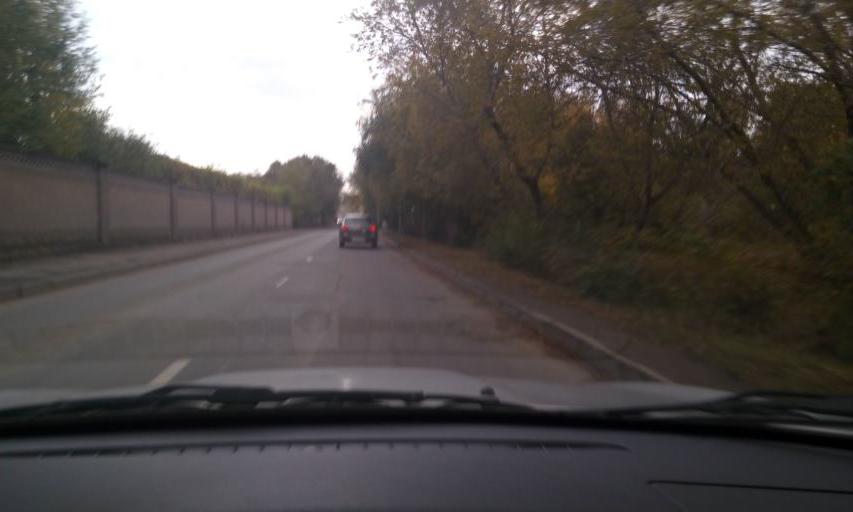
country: KZ
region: Astana Qalasy
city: Astana
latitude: 51.1425
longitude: 71.4317
